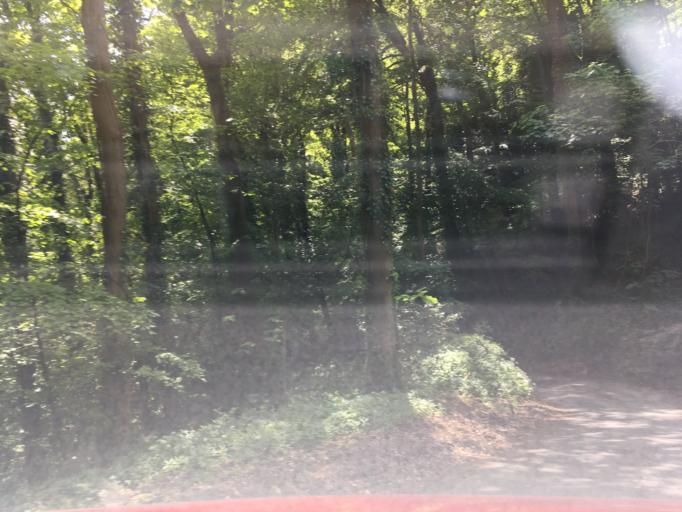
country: GB
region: England
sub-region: Gloucestershire
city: Dursley
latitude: 51.6684
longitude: -2.3367
